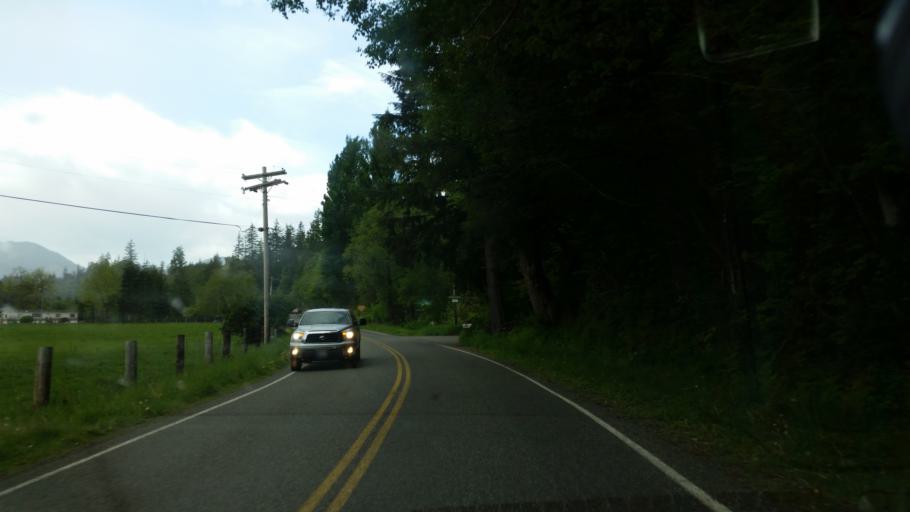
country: US
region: Washington
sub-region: Mason County
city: Shelton
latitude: 47.3212
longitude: -123.2697
